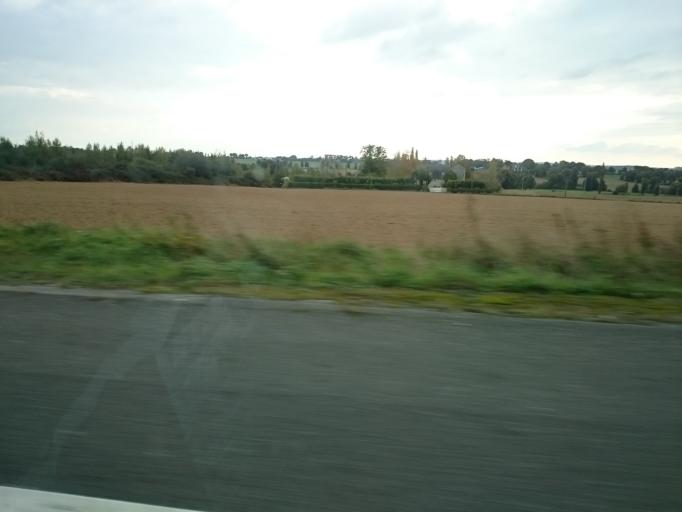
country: FR
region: Brittany
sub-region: Departement d'Ille-et-Vilaine
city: Bedee
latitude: 48.1859
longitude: -1.9860
